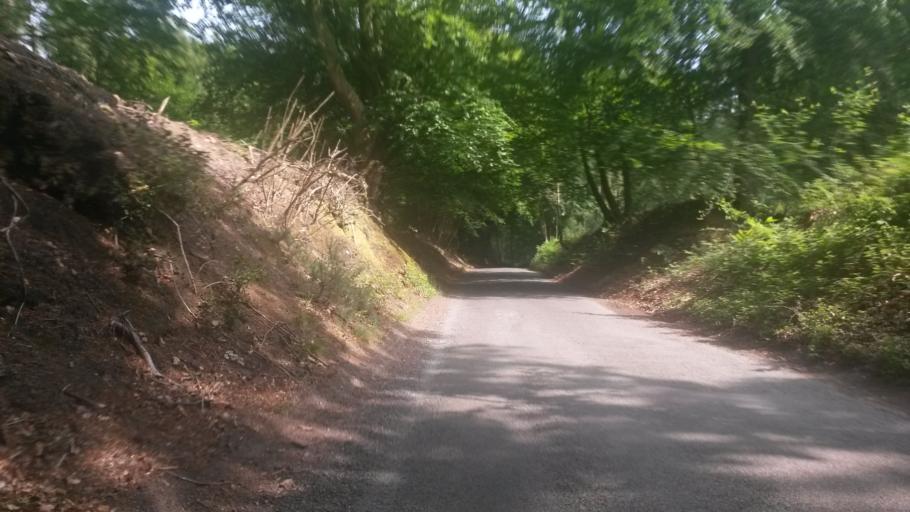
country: GB
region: England
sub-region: Surrey
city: Haslemere
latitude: 51.0721
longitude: -0.6900
